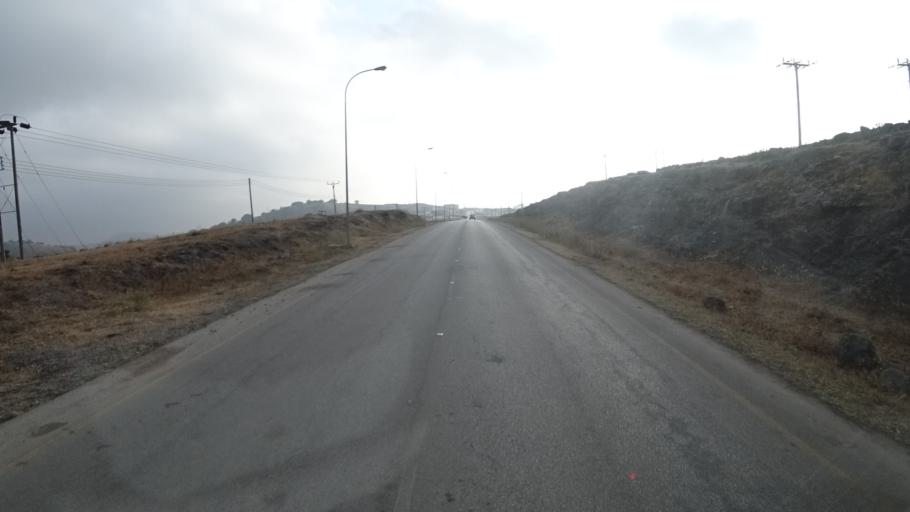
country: OM
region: Zufar
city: Salalah
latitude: 17.1236
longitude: 53.9940
